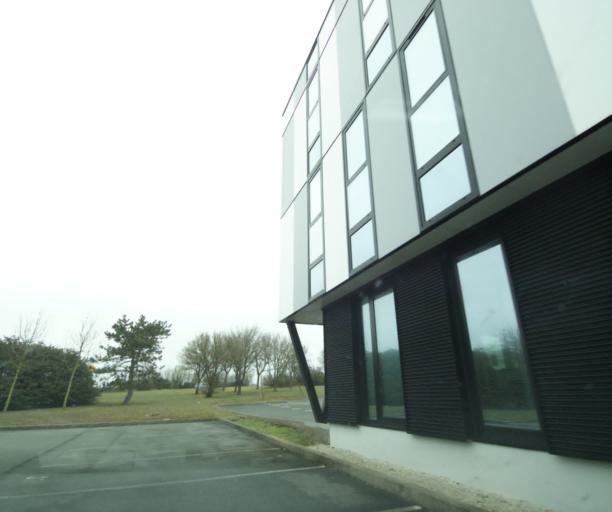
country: FR
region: Poitou-Charentes
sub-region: Departement de la Charente-Maritime
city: Lagord
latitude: 46.1907
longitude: -1.1446
